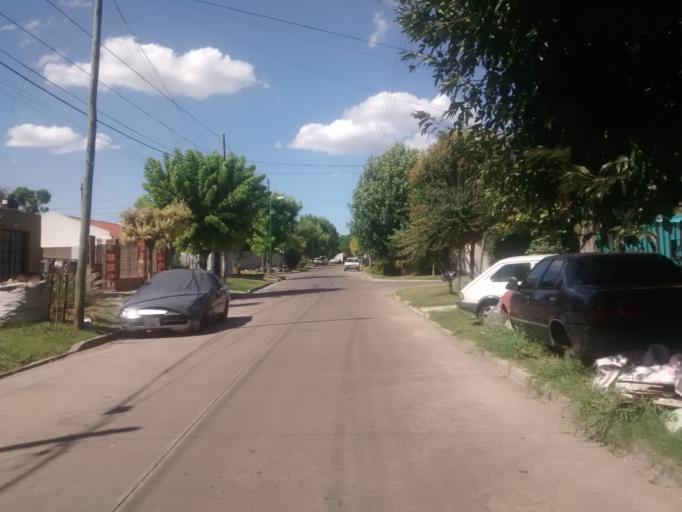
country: AR
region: Buenos Aires
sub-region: Partido de La Plata
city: La Plata
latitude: -34.9363
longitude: -57.9172
